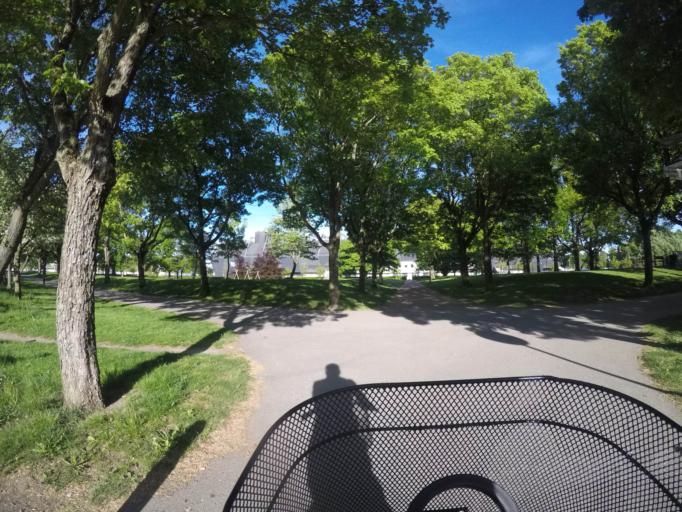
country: SE
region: Skane
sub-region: Malmo
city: Malmoe
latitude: 55.5843
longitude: 12.9847
